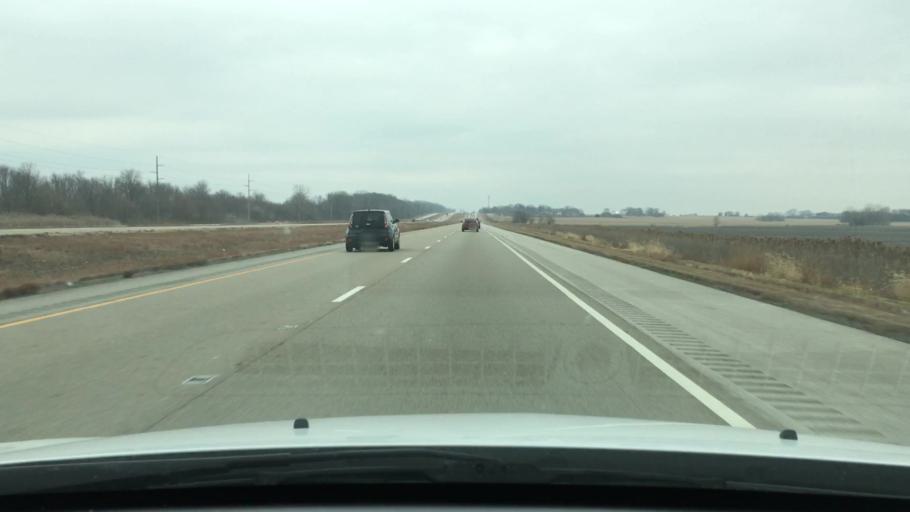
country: US
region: Illinois
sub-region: Logan County
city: Atlanta
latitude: 40.2265
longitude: -89.2696
